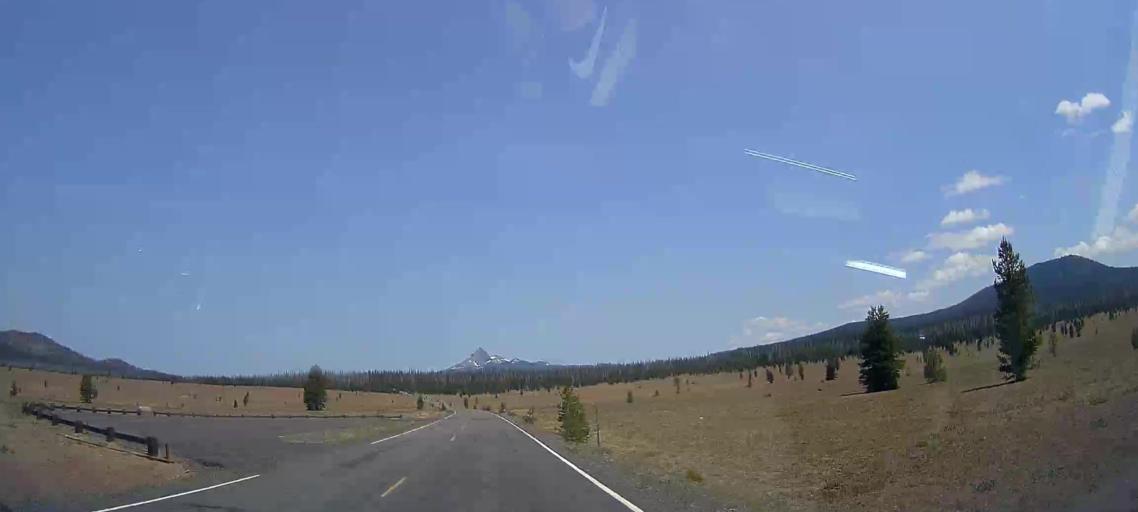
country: US
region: Oregon
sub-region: Lane County
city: Oakridge
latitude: 43.0276
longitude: -122.1192
